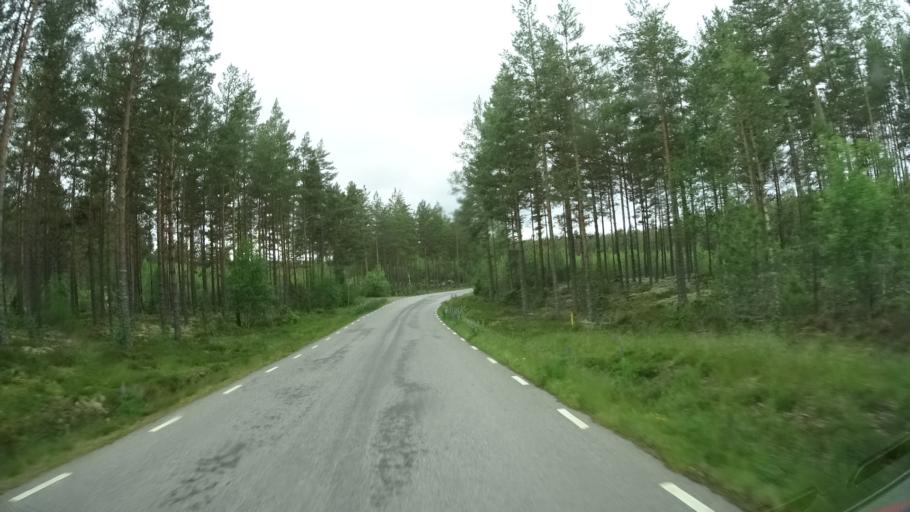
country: SE
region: Joenkoeping
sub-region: Eksjo Kommun
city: Mariannelund
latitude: 57.7012
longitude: 15.6264
